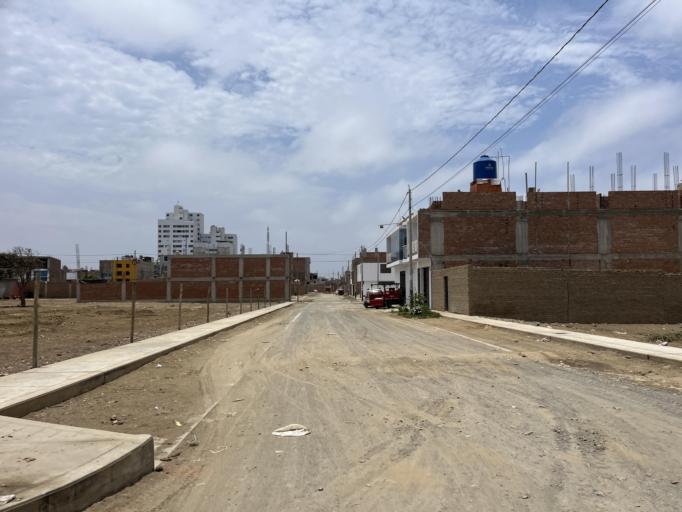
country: PE
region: La Libertad
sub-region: Provincia de Trujillo
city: La Esperanza
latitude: -8.0868
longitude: -79.0500
